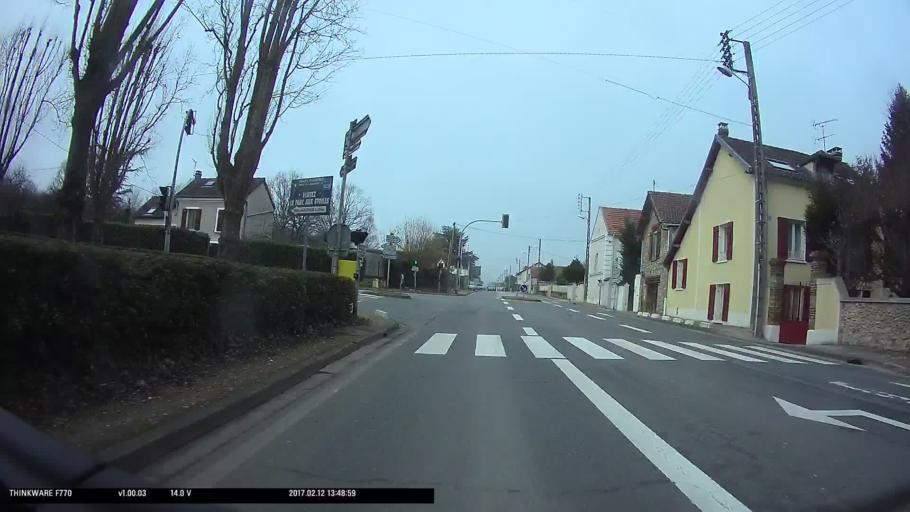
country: FR
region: Ile-de-France
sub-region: Departement des Yvelines
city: Triel-sur-Seine
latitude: 49.0026
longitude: 2.0119
